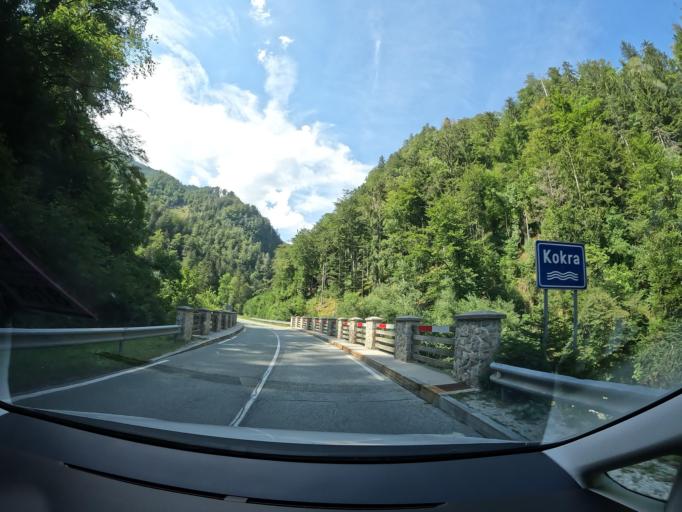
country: SI
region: Trzic
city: Trzic
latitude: 46.3914
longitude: 14.3525
